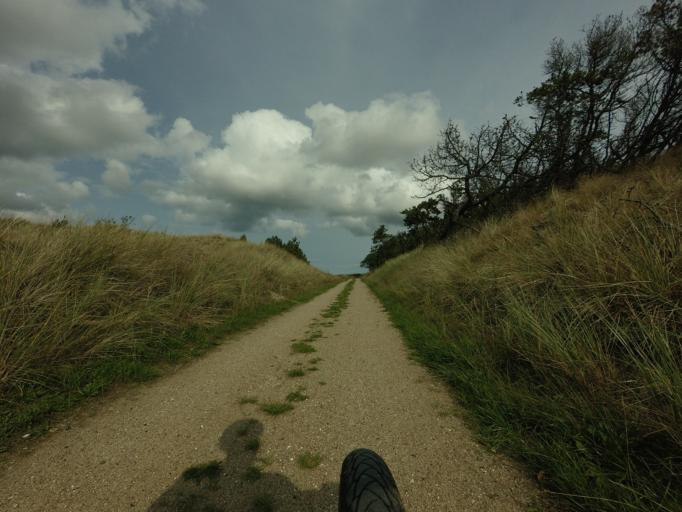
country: DK
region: North Denmark
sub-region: Frederikshavn Kommune
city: Strandby
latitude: 57.6325
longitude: 10.3995
